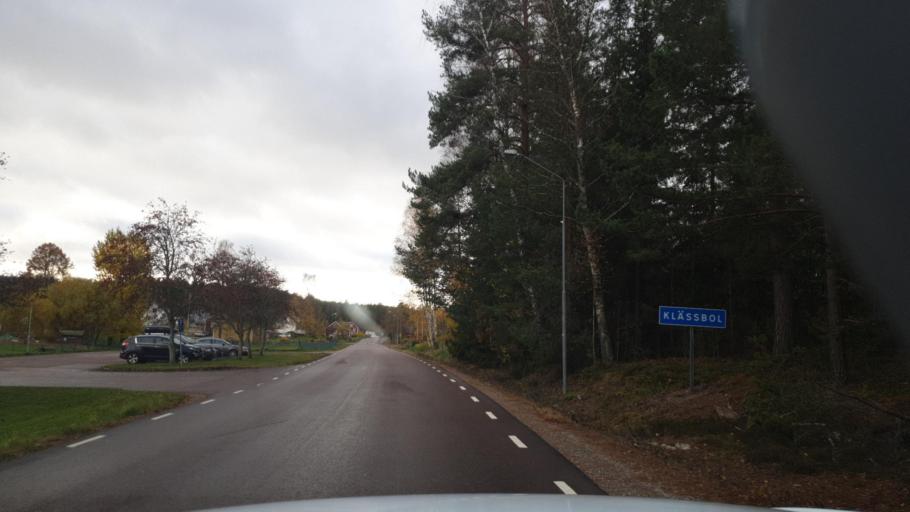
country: SE
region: Vaermland
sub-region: Arvika Kommun
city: Arvika
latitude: 59.5413
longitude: 12.7463
